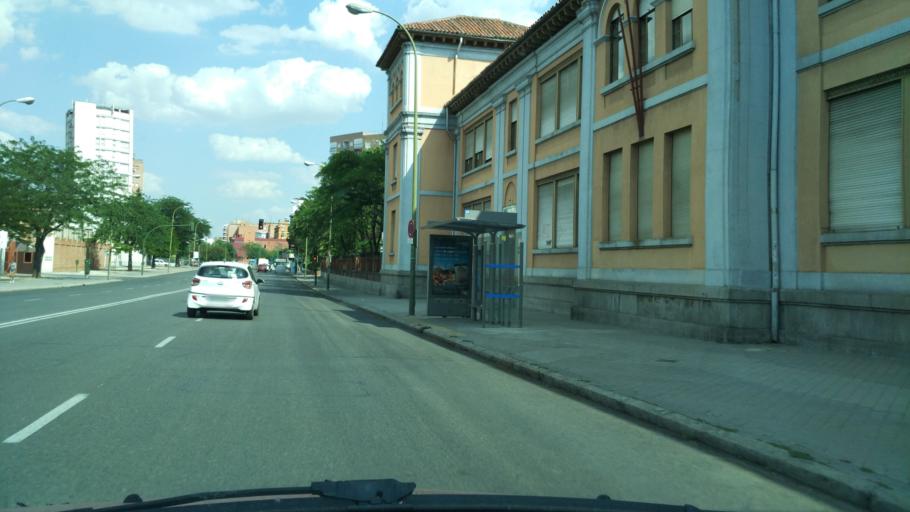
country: ES
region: Madrid
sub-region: Provincia de Madrid
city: Tetuan de las Victorias
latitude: 40.4585
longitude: -3.7156
